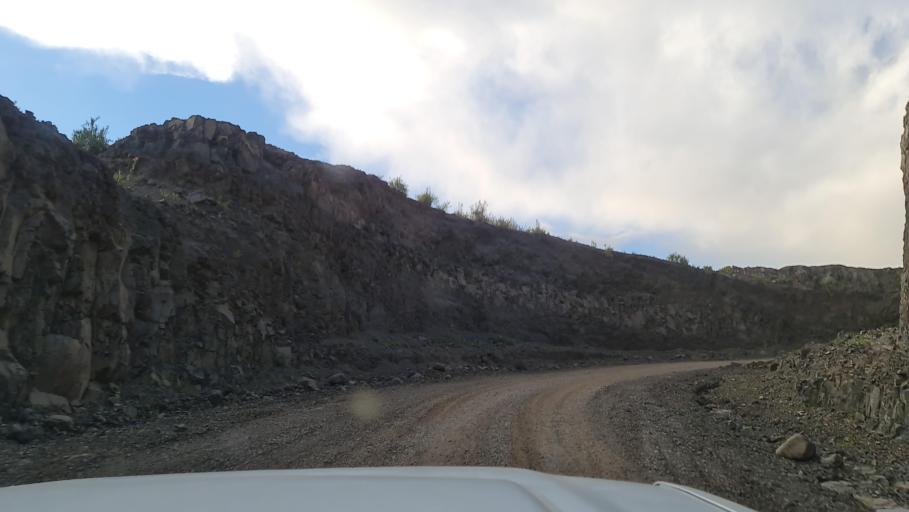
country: ET
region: Amhara
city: Debark'
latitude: 13.0116
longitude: 38.0472
